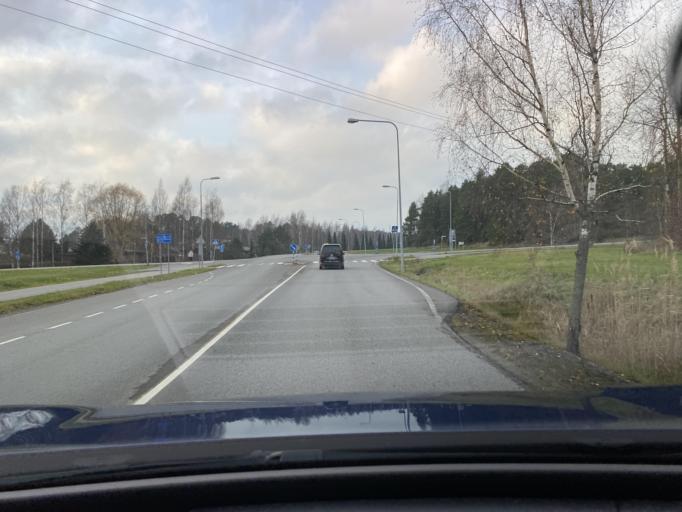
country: FI
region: Varsinais-Suomi
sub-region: Turku
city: Naantali
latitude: 60.4750
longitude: 22.0492
